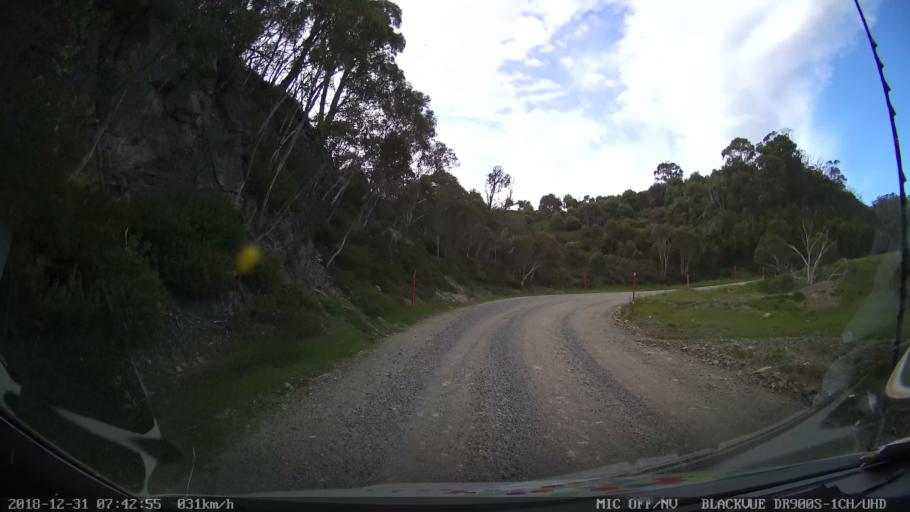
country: AU
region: New South Wales
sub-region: Snowy River
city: Jindabyne
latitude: -36.3587
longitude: 148.4077
